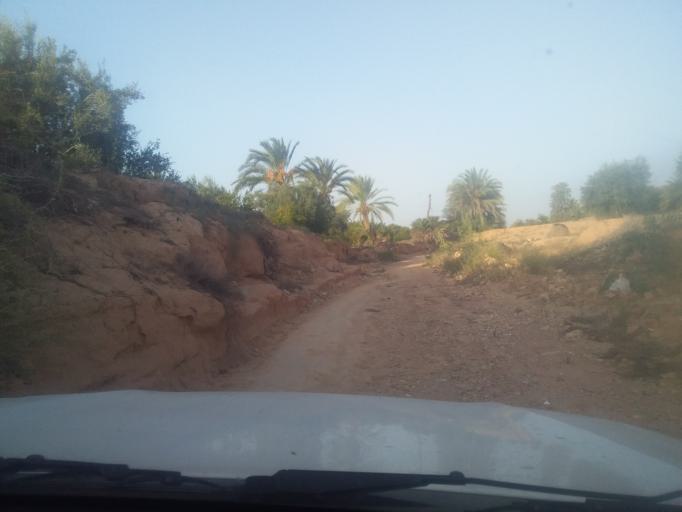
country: TN
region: Qabis
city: Gabes
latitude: 33.6293
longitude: 10.2987
